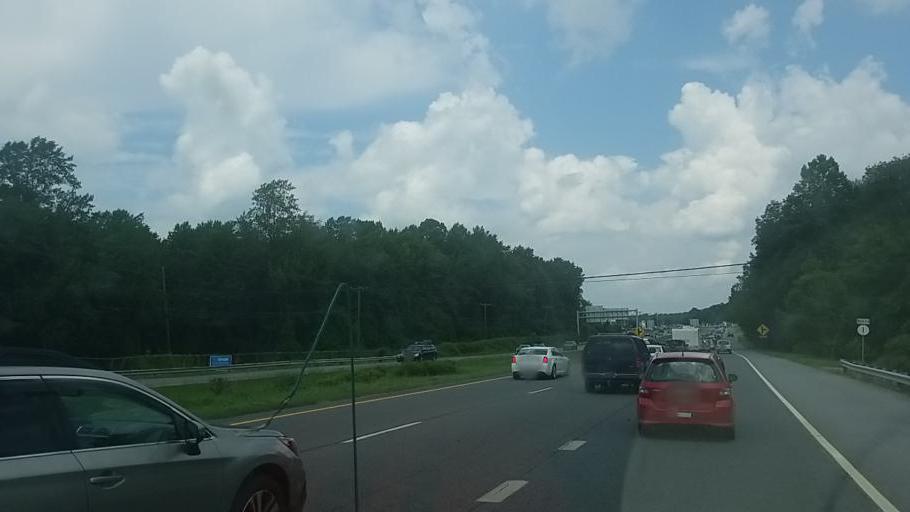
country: US
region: Delaware
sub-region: Sussex County
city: Milford
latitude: 38.9422
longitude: -75.4270
